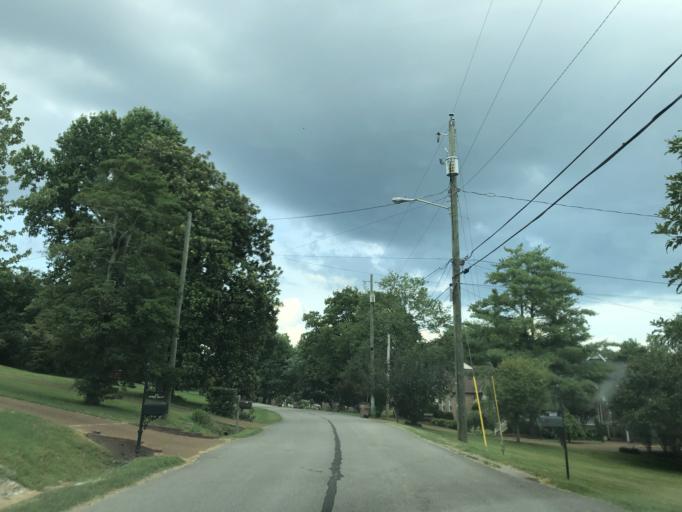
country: US
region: Tennessee
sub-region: Davidson County
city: Lakewood
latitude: 36.1643
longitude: -86.6729
